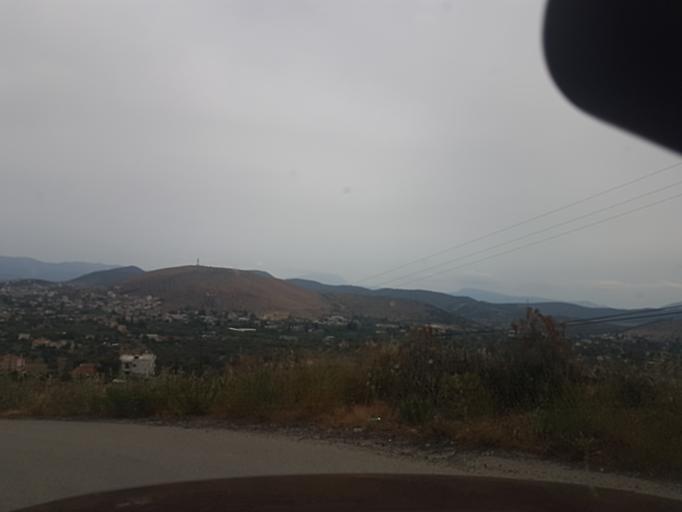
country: GR
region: Central Greece
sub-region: Nomos Evvoias
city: Chalkida
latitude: 38.4620
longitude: 23.6280
